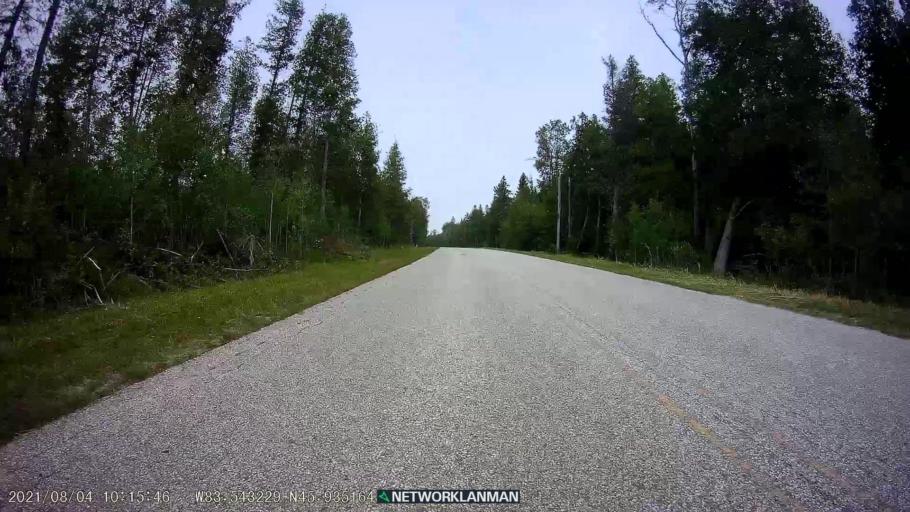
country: CA
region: Ontario
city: Thessalon
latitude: 45.9350
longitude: -83.5431
